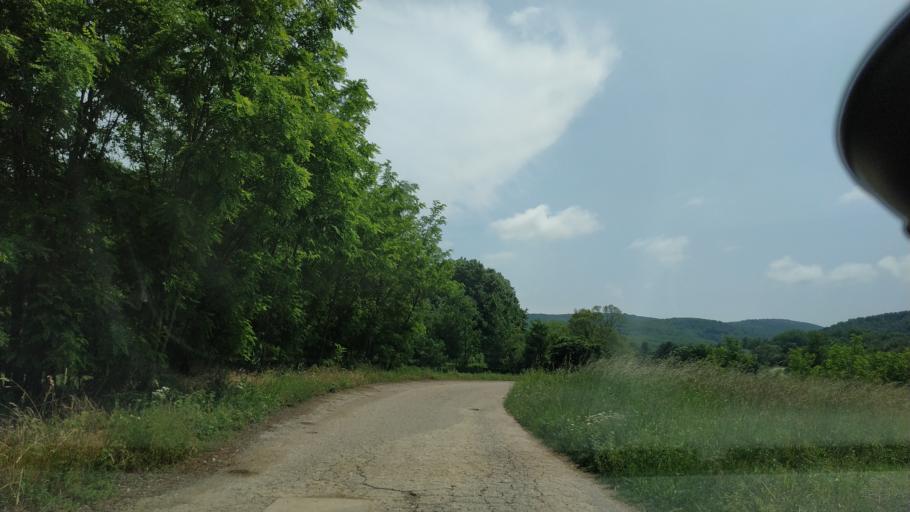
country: RS
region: Central Serbia
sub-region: Nisavski Okrug
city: Aleksinac
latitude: 43.4209
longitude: 21.7175
